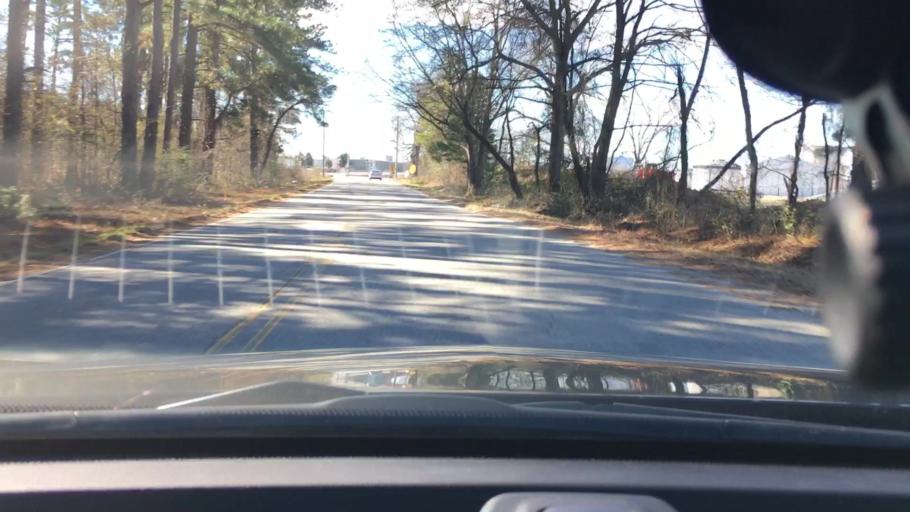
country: US
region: South Carolina
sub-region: Spartanburg County
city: Spartanburg
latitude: 34.9254
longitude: -81.8614
